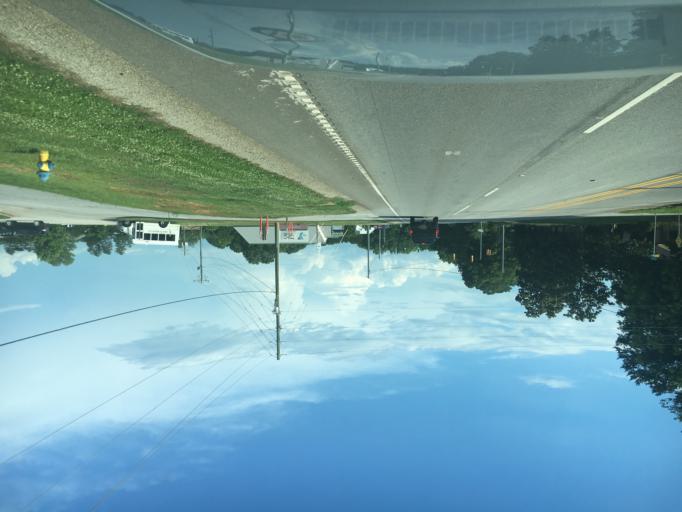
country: US
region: South Carolina
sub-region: Greenville County
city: Simpsonville
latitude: 34.7733
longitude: -82.2569
